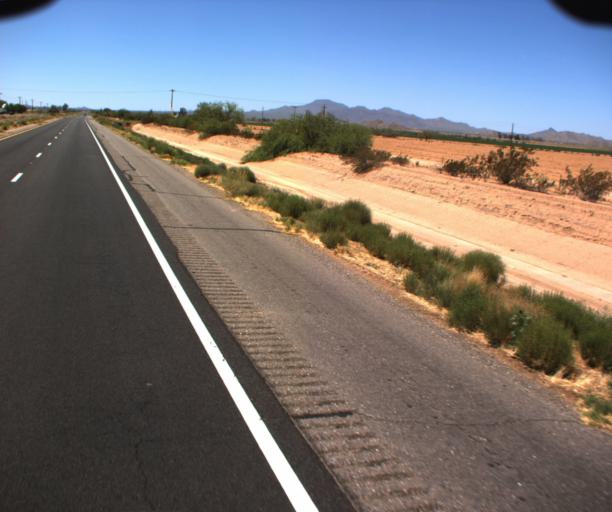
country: US
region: Arizona
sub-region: Pinal County
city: Maricopa
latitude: 32.9180
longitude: -112.0497
